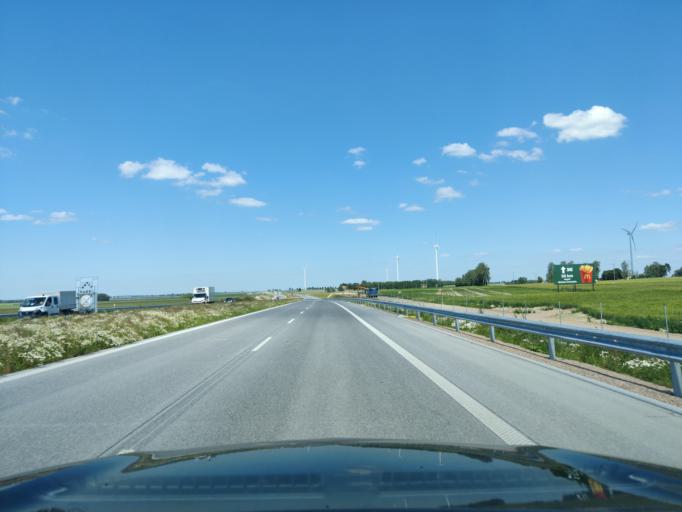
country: PL
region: Masovian Voivodeship
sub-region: Powiat mlawski
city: Wisniewo
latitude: 53.0356
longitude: 20.3541
